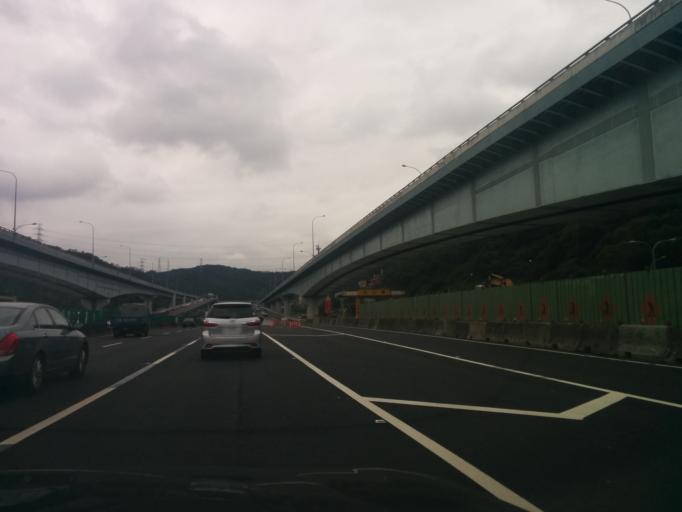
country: TW
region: Taipei
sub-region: Taipei
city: Banqiao
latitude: 25.0623
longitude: 121.4164
